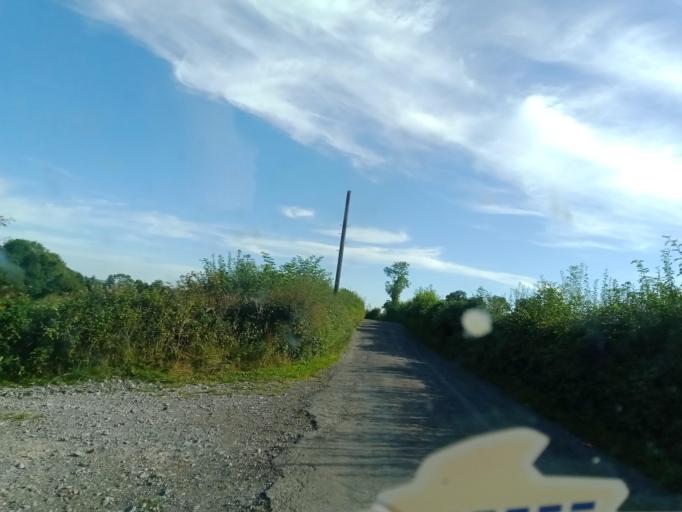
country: IE
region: Leinster
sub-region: Kilkenny
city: Ballyragget
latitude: 52.7676
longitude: -7.3920
